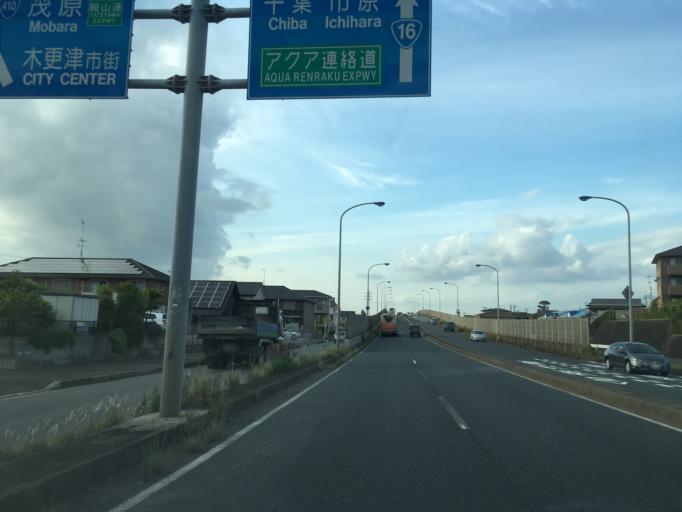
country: JP
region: Chiba
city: Kisarazu
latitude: 35.3832
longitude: 139.9420
